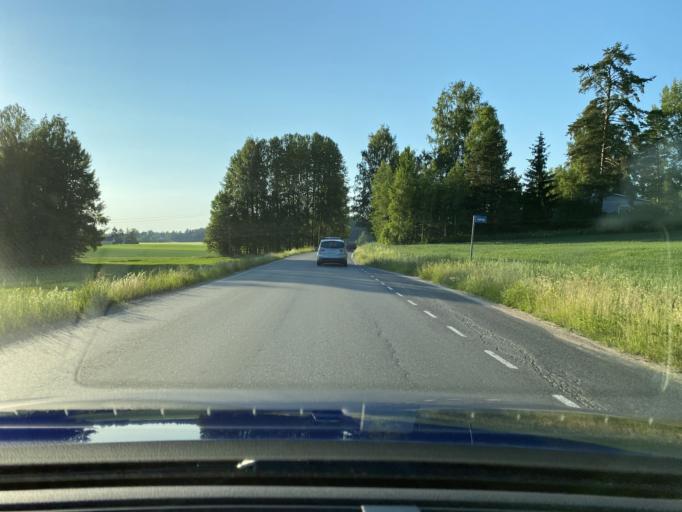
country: FI
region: Haeme
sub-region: Haemeenlinna
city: Tervakoski
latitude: 60.7321
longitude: 24.6710
